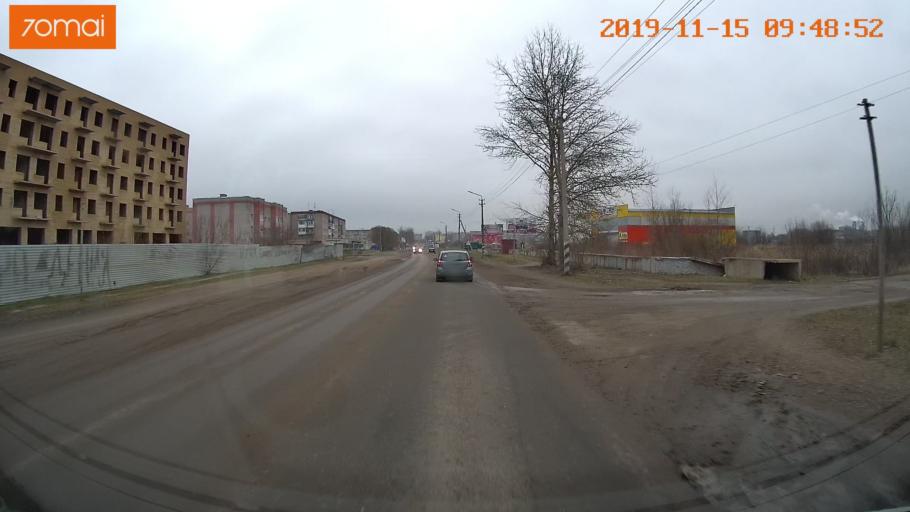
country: RU
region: Vologda
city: Sheksna
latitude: 59.2257
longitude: 38.5137
